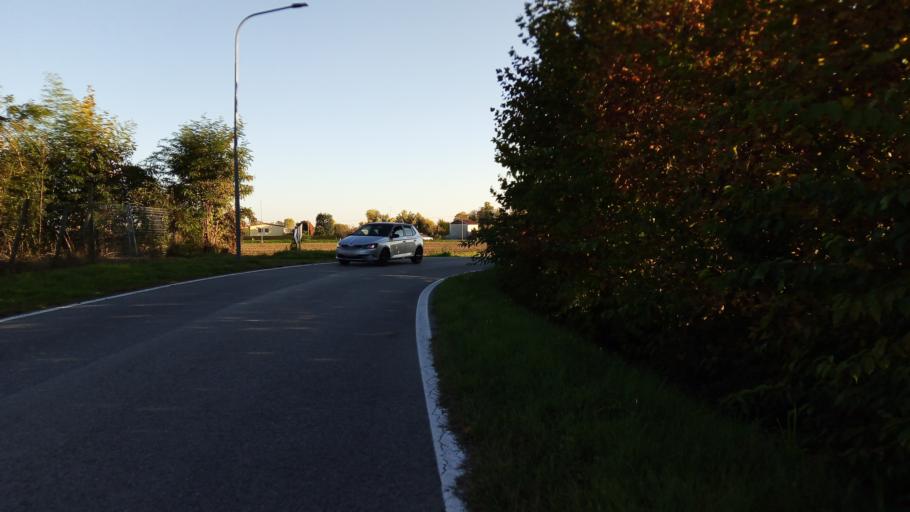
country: IT
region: Veneto
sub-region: Provincia di Padova
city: Abano Terme
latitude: 45.3512
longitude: 11.8021
